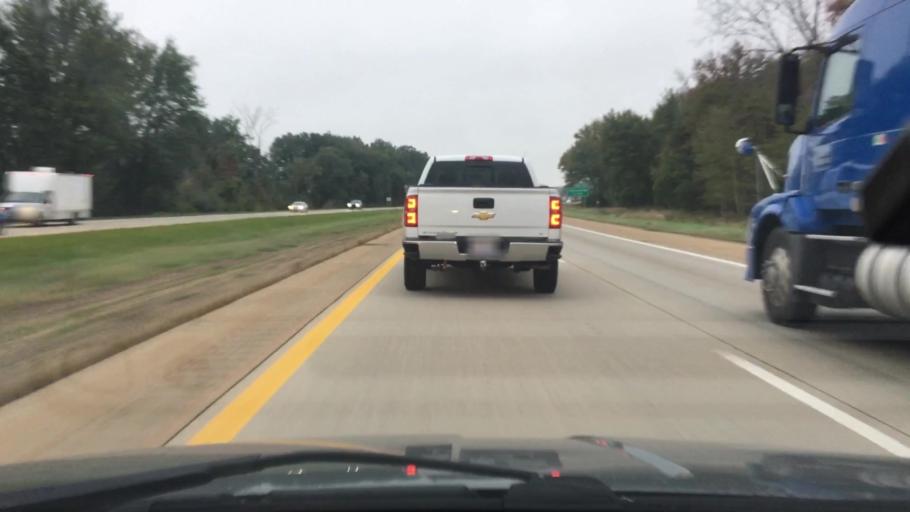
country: US
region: Michigan
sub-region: Jackson County
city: Concord
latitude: 42.2629
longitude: -84.6289
